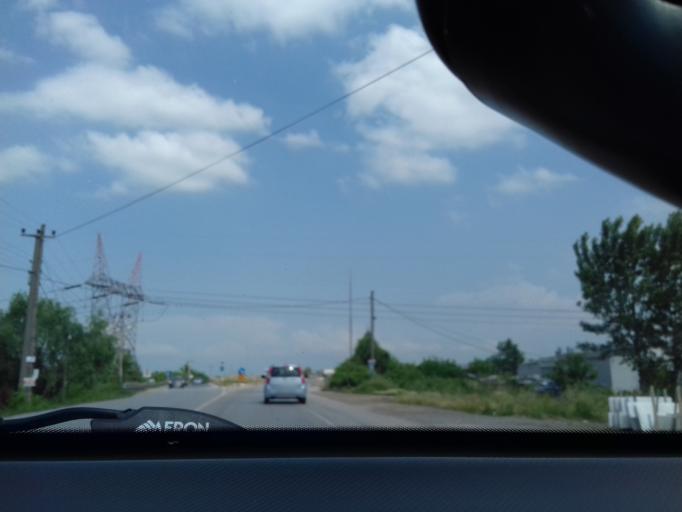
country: TR
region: Sakarya
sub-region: Merkez
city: Sapanca
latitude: 40.7136
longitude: 30.3433
